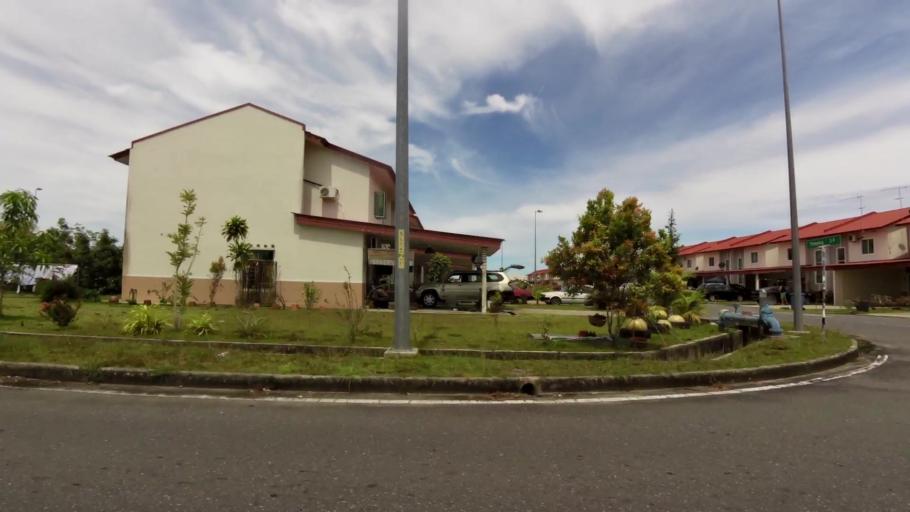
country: BN
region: Belait
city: Kuala Belait
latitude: 4.5876
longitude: 114.2707
